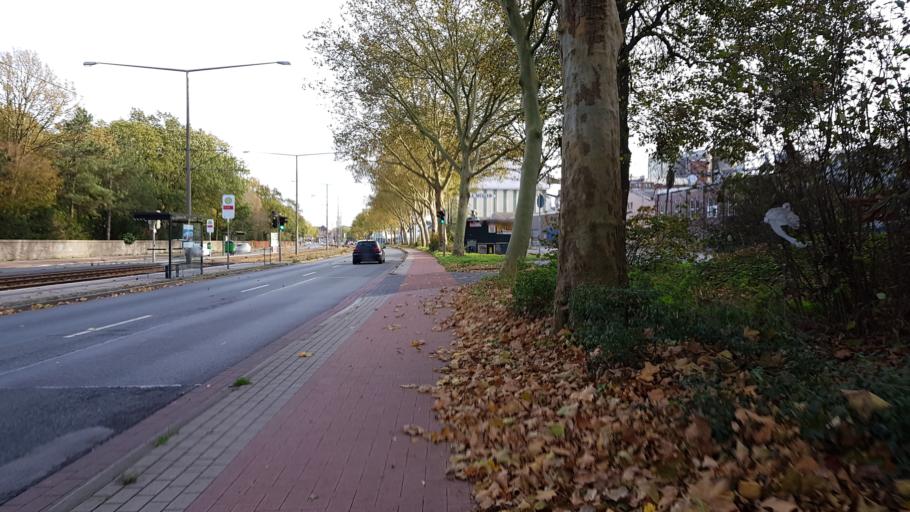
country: DE
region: Bremen
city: Bremen
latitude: 53.1045
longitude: 8.7684
